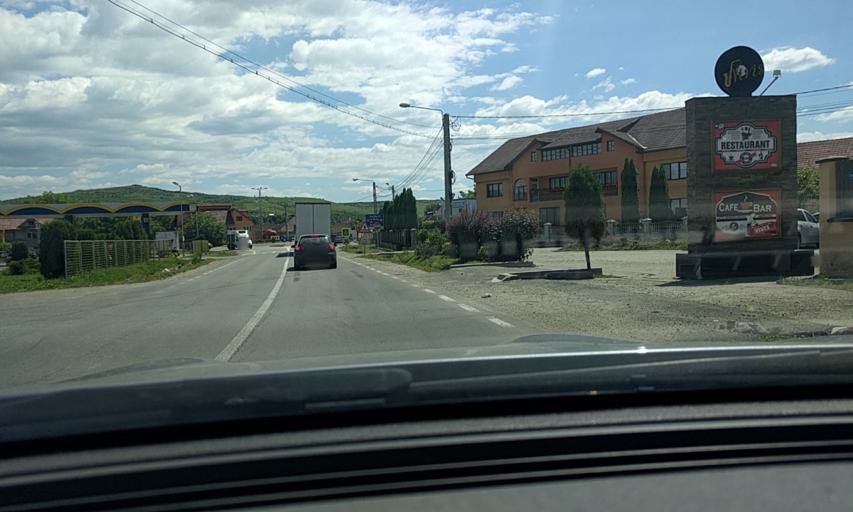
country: RO
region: Bistrita-Nasaud
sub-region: Municipiul Bistrita
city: Viisoara
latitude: 47.1093
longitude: 24.4541
